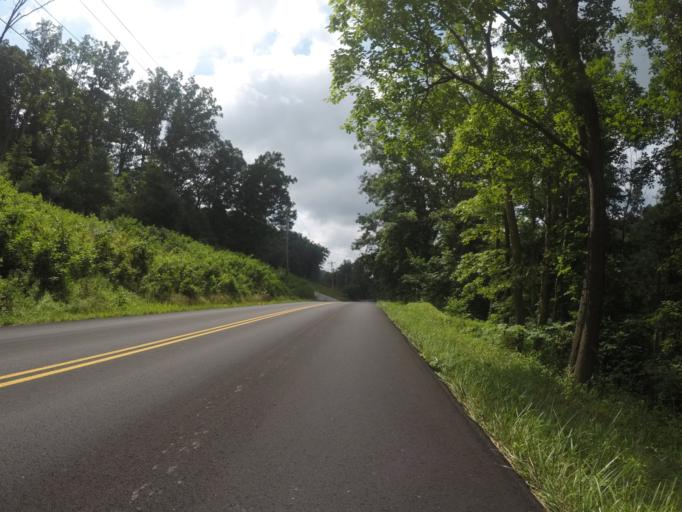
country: US
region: Kentucky
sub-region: Boyd County
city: Meads
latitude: 38.4026
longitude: -82.6580
